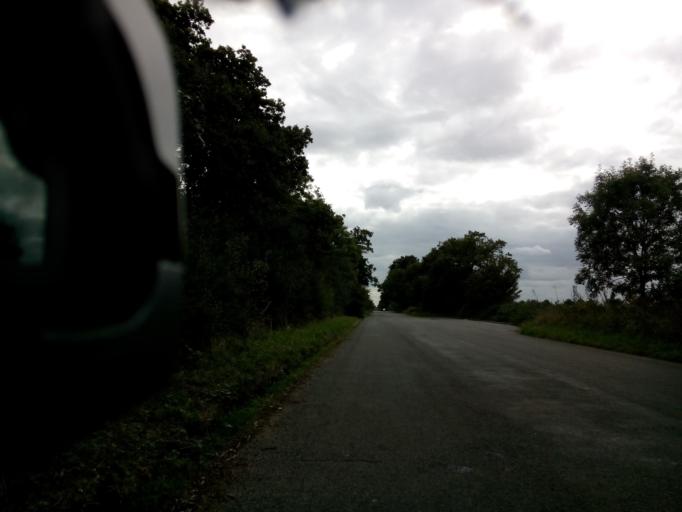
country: GB
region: England
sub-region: Suffolk
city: Capel Saint Mary
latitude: 52.0131
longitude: 1.0663
